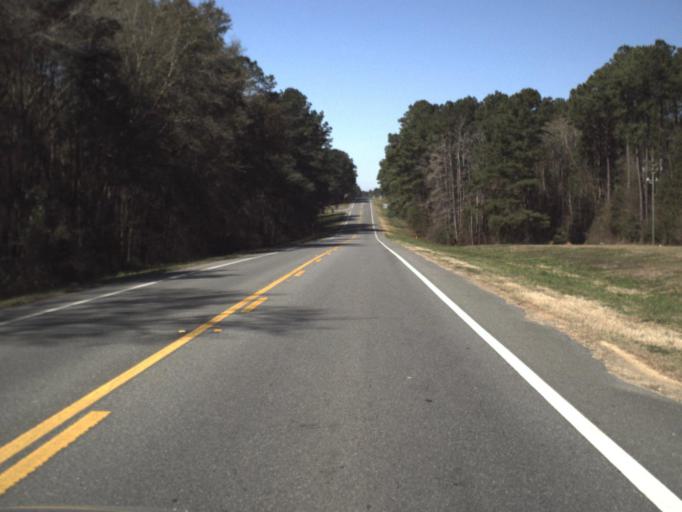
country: US
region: Florida
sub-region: Jackson County
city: Sneads
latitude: 30.7114
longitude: -84.9425
